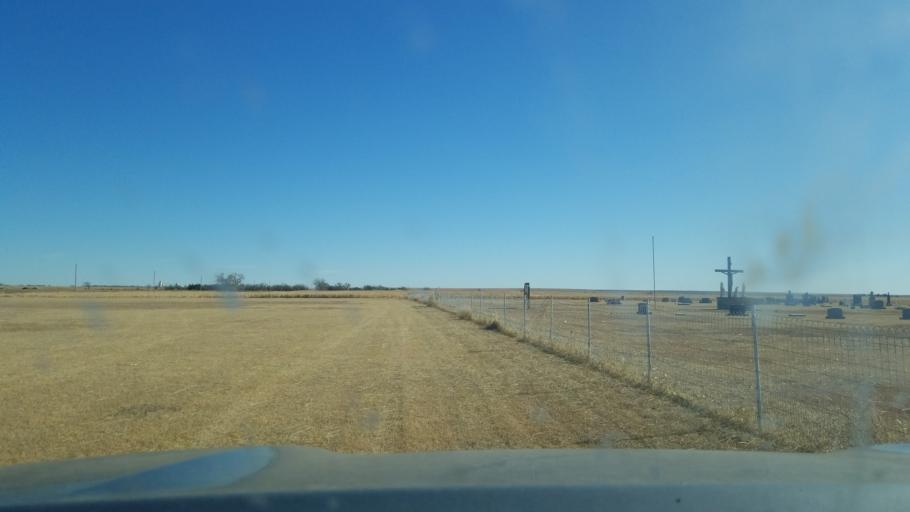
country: US
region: Kansas
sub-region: Ness County
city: Ness City
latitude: 38.5668
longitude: -99.6418
